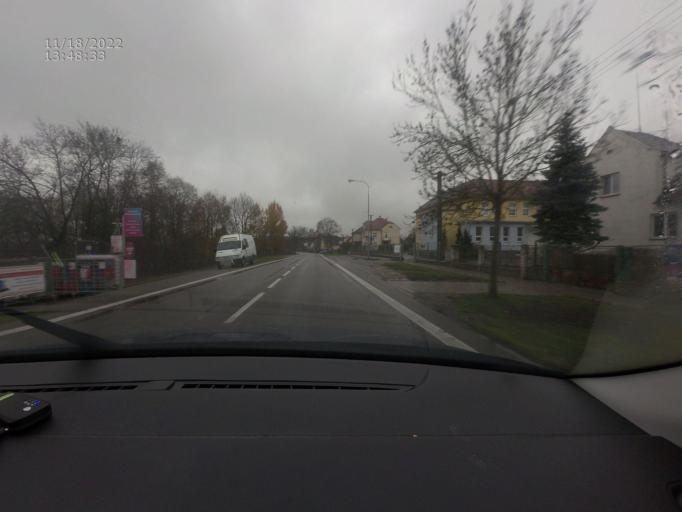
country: CZ
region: Jihocesky
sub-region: Okres Strakonice
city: Blatna
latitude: 49.4179
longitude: 13.8849
